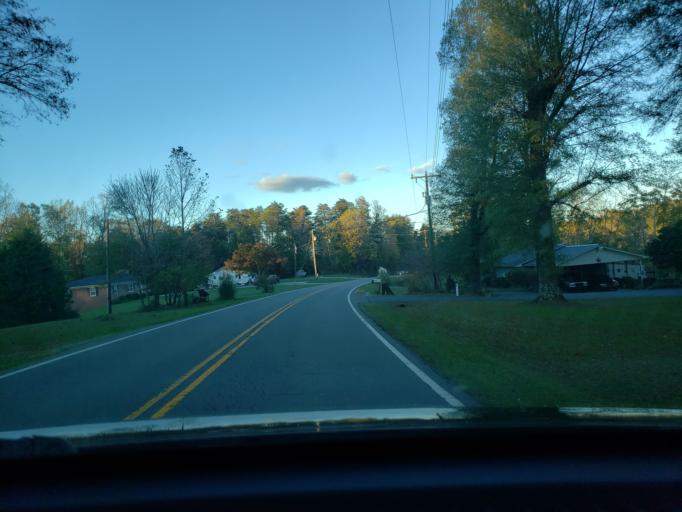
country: US
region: North Carolina
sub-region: Stokes County
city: Danbury
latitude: 36.3546
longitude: -80.2155
